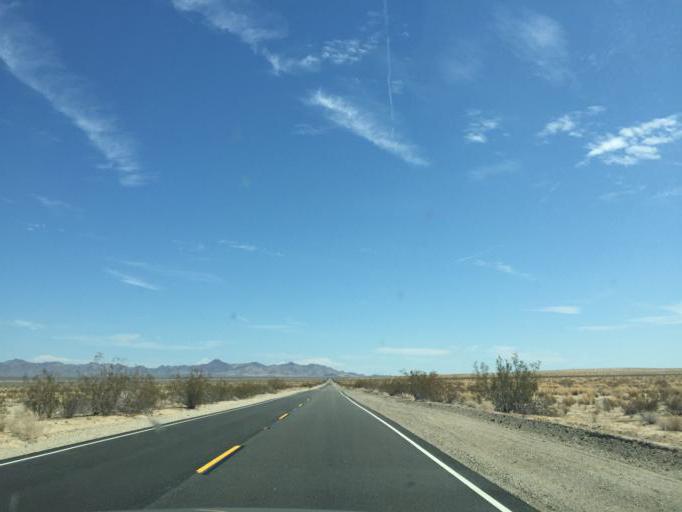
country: US
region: California
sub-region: Riverside County
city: Mesa Verde
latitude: 34.1011
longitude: -114.9922
